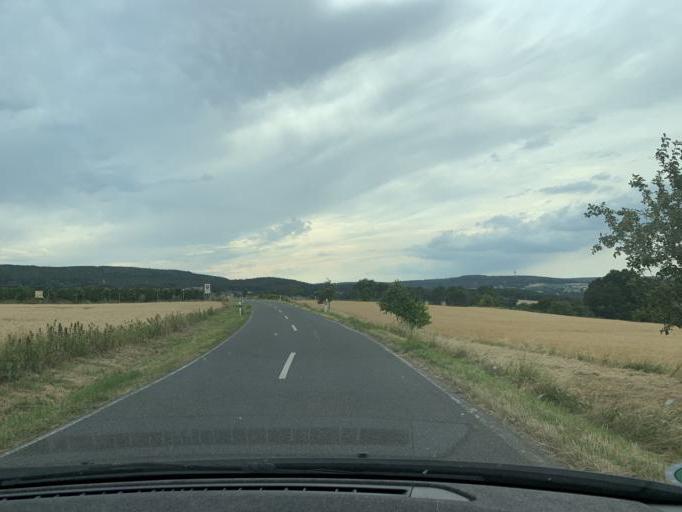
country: DE
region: North Rhine-Westphalia
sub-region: Regierungsbezirk Koln
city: Nideggen
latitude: 50.7184
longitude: 6.4889
